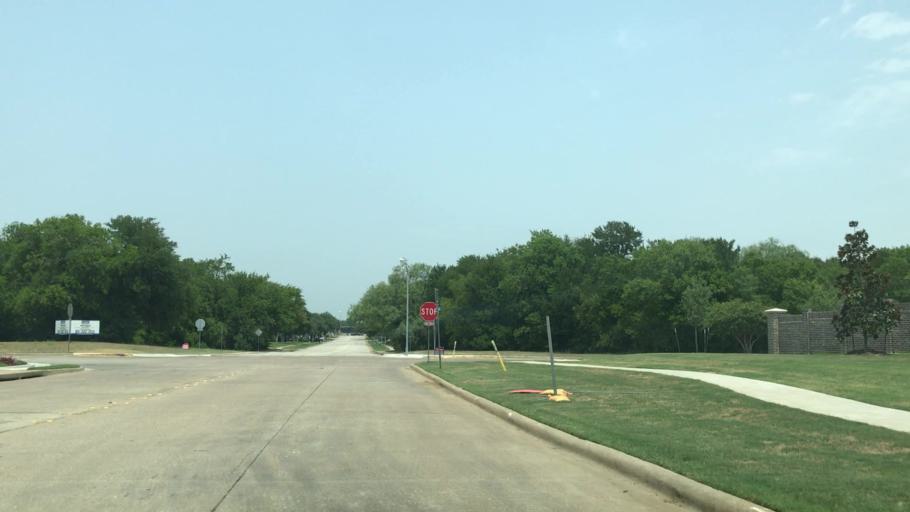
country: US
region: Texas
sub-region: Tarrant County
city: Euless
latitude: 32.8461
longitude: -97.0727
